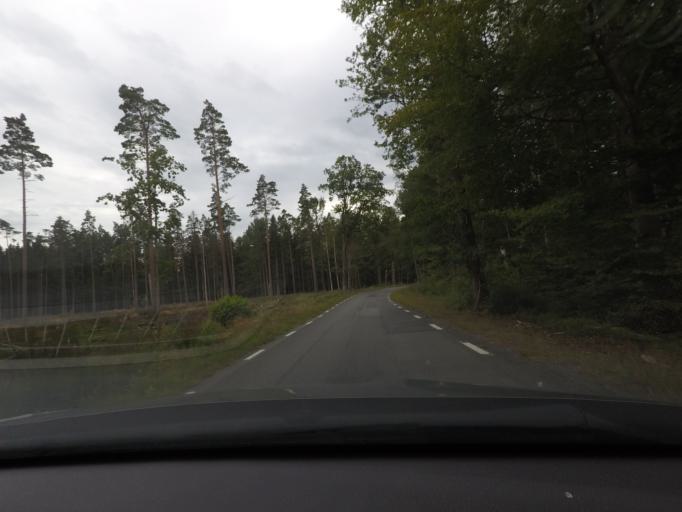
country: SE
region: Kronoberg
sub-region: Markaryds Kommun
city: Markaryd
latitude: 56.4171
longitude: 13.7120
